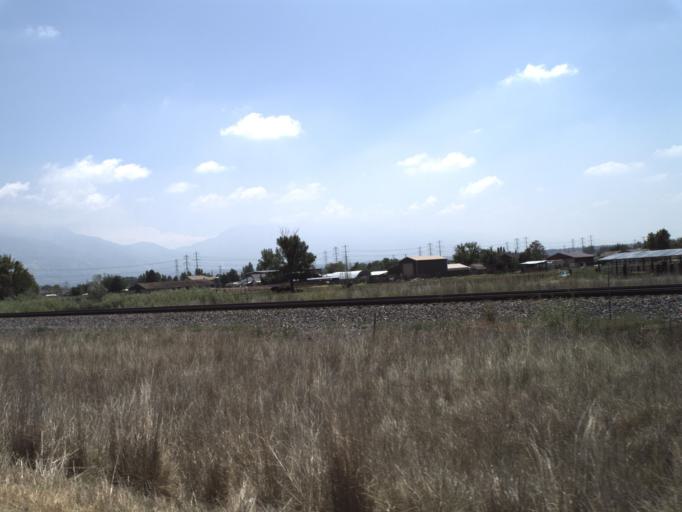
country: US
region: Utah
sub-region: Weber County
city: West Haven
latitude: 41.2444
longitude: -112.0718
